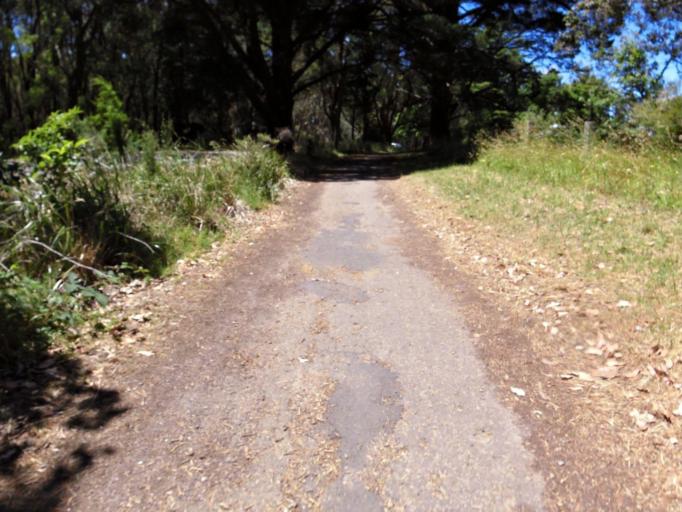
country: AU
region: Victoria
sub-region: Mornington Peninsula
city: Safety Beach
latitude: -38.3723
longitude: 145.0211
